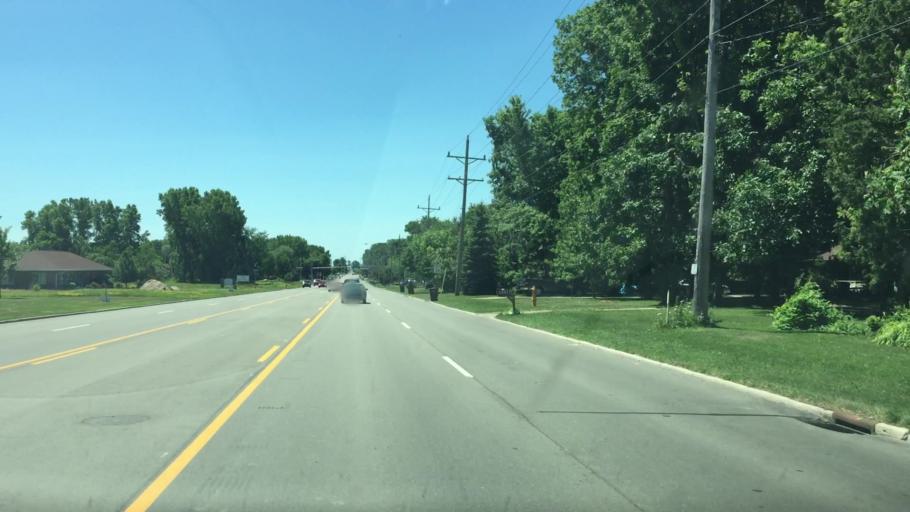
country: US
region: Wisconsin
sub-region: Outagamie County
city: Appleton
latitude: 44.2224
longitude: -88.4042
